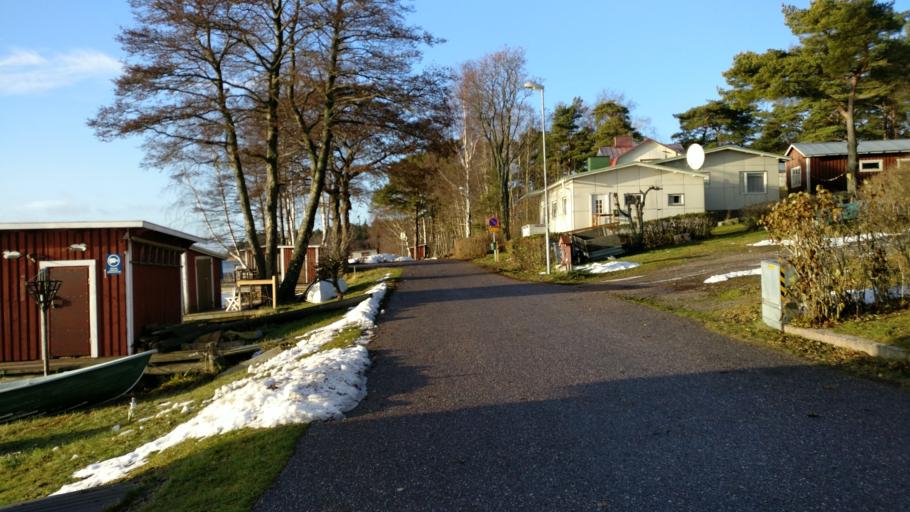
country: FI
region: Uusimaa
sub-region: Raaseporin
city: Hanko
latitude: 59.8363
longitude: 22.9304
